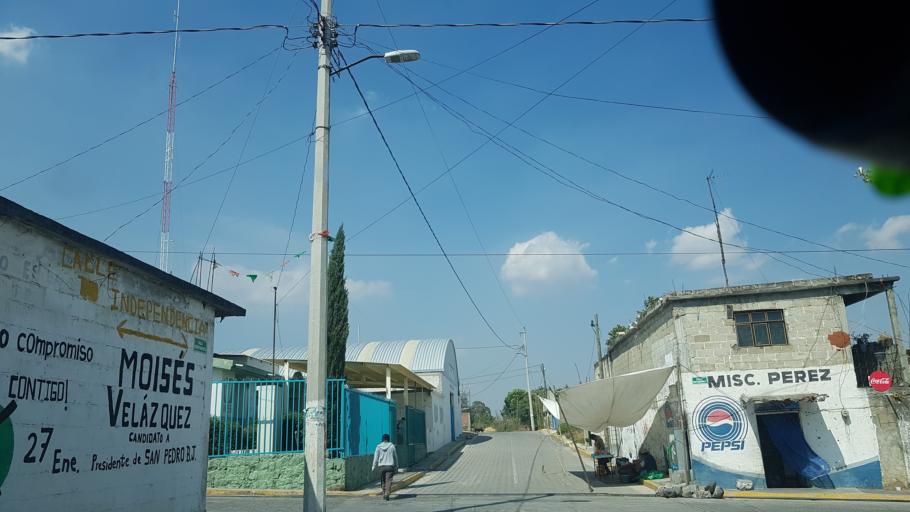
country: MX
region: Puebla
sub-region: Atlixco
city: San Pedro Benito Juarez
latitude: 18.9486
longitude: -98.5492
